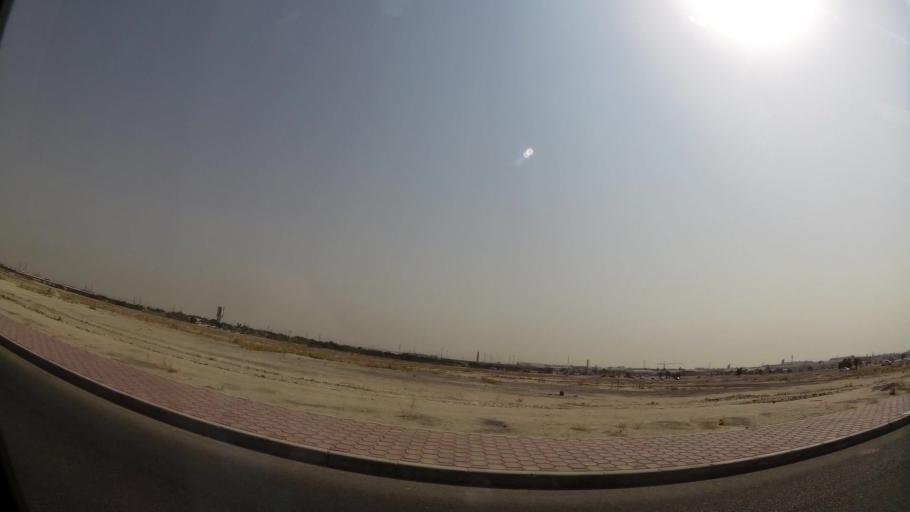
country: KW
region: Muhafazat al Jahra'
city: Al Jahra'
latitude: 29.3193
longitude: 47.7416
